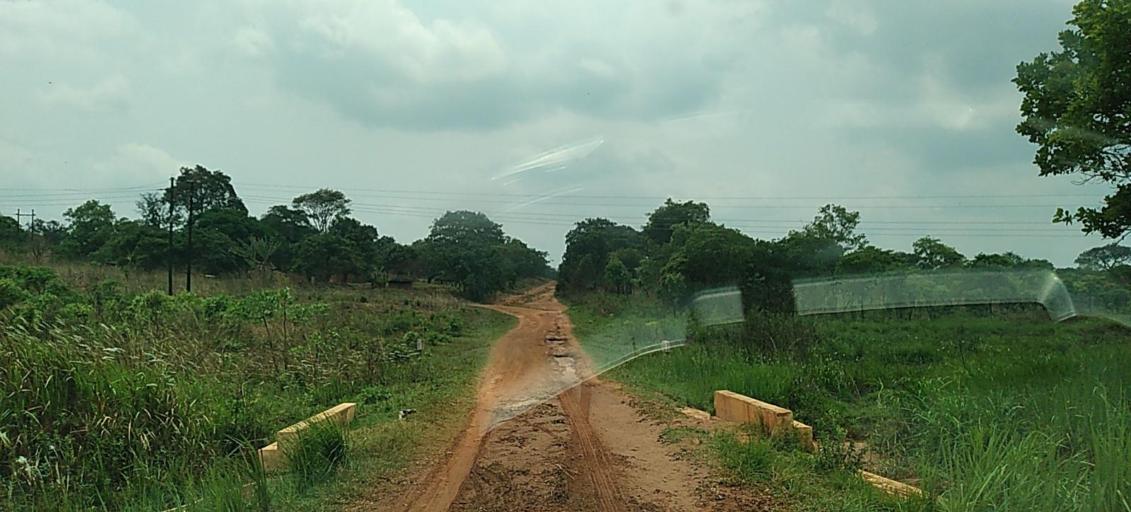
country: ZM
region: North-Western
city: Mwinilunga
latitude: -11.5363
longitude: 24.7832
